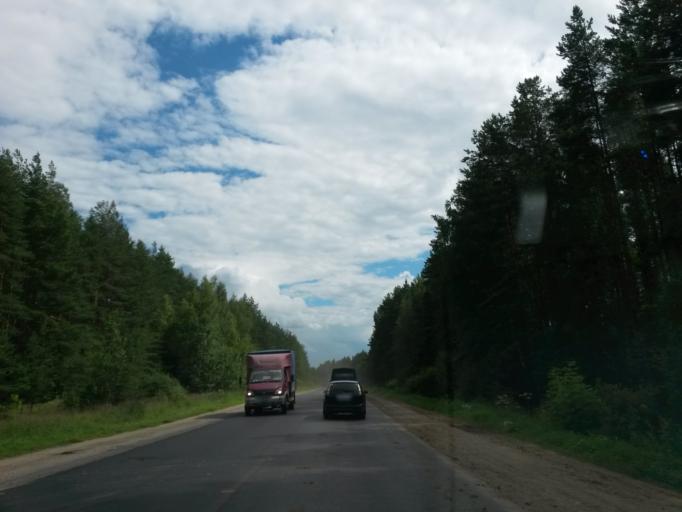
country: RU
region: Ivanovo
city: Novo-Talitsy
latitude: 57.0186
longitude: 40.7795
